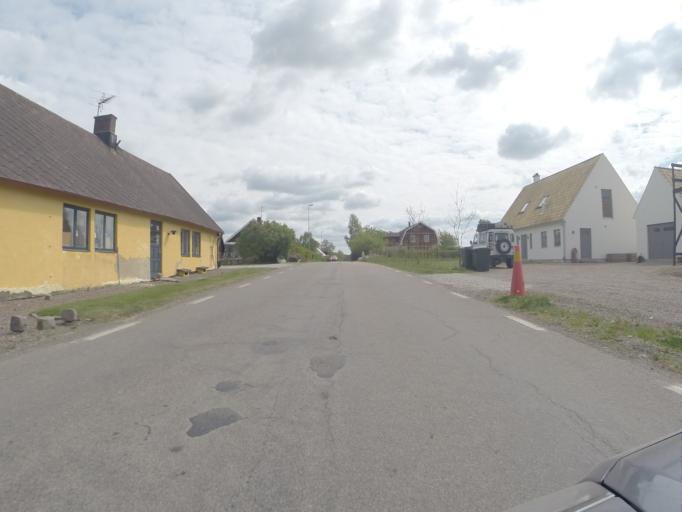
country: SE
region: Skane
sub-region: Helsingborg
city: Morarp
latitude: 56.0750
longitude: 12.8504
